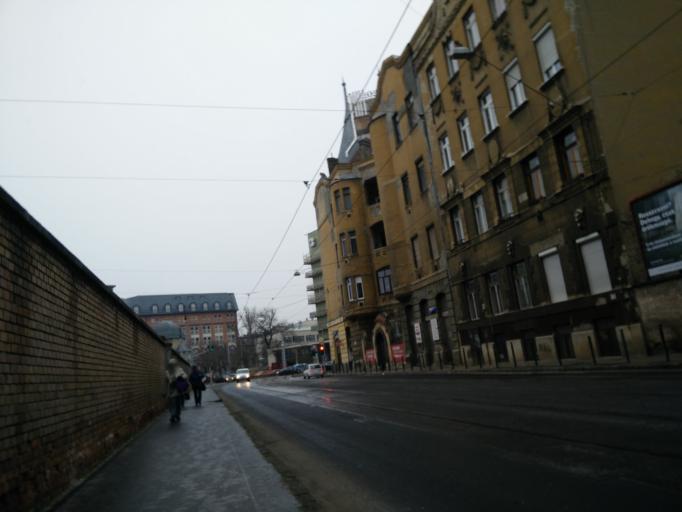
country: HU
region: Budapest
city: Budapest VII. keruelet
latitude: 47.4981
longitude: 19.0826
